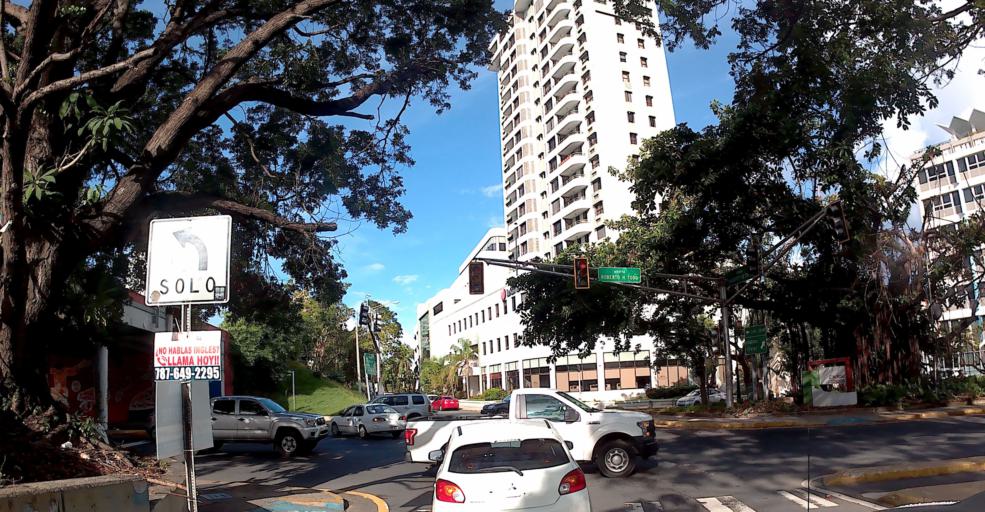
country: PR
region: San Juan
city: San Juan
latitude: 18.4534
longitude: -66.0733
